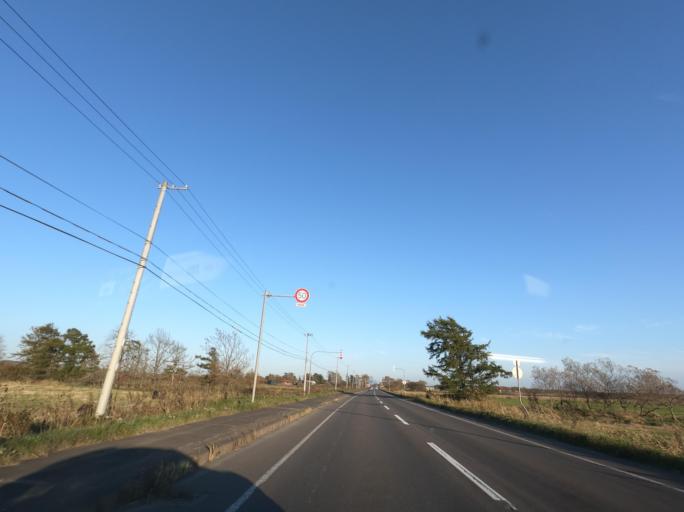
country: JP
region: Hokkaido
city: Kushiro
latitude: 43.0553
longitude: 144.2882
